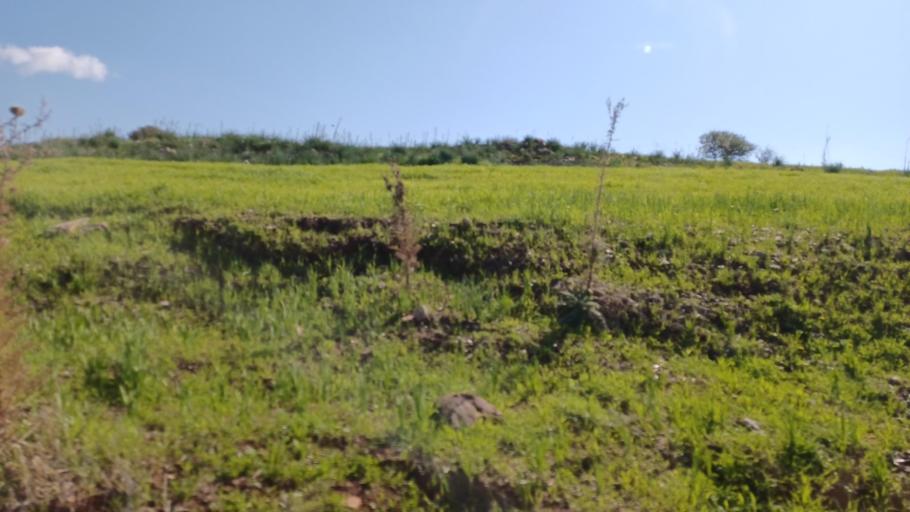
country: CY
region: Pafos
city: Mesogi
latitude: 34.7559
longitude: 32.5341
